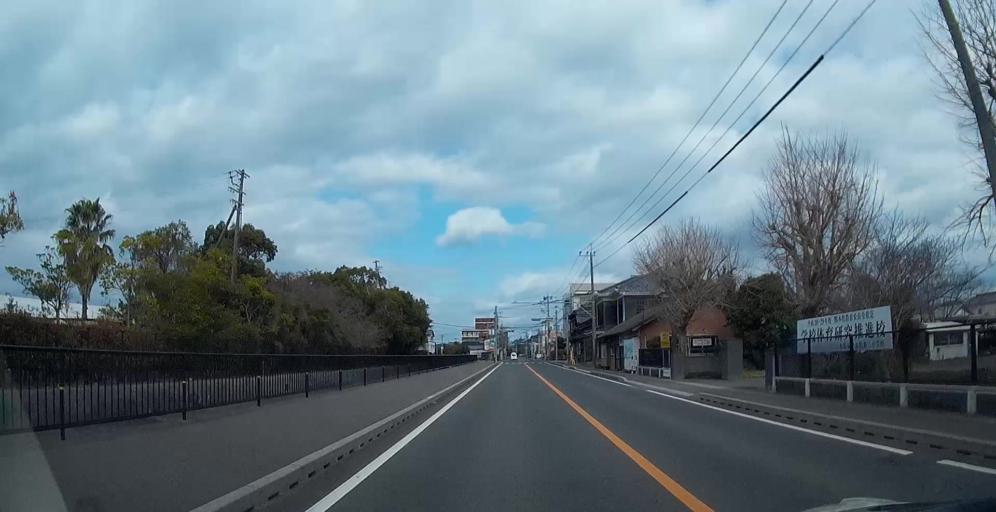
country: JP
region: Kumamoto
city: Minamata
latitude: 32.2097
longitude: 130.3961
